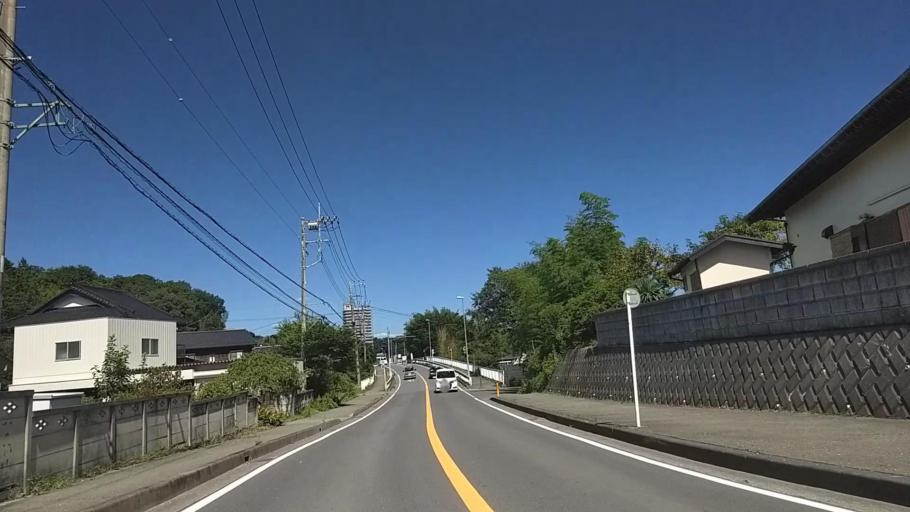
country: JP
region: Kanagawa
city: Zama
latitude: 35.5376
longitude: 139.3274
